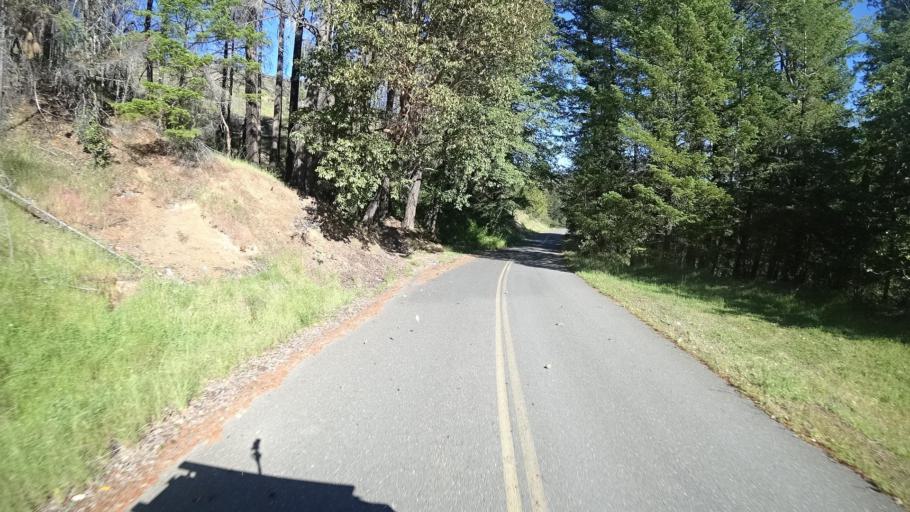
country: US
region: California
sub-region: Lake County
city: Upper Lake
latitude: 39.4064
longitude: -122.9736
